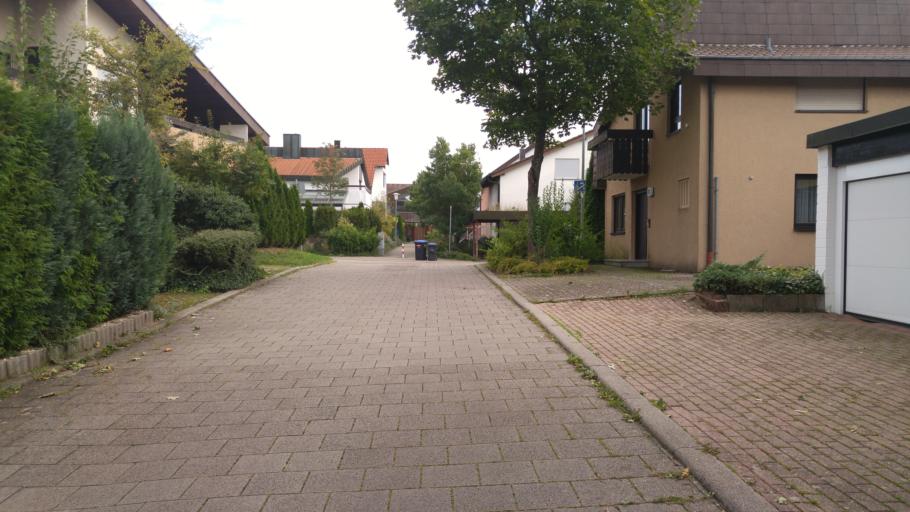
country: DE
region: Baden-Wuerttemberg
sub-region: Regierungsbezirk Stuttgart
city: Leonberg
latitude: 48.8088
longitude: 9.0061
